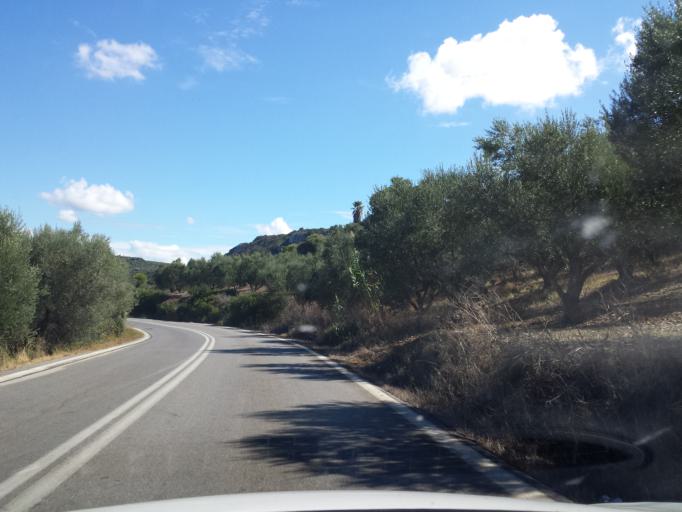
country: GR
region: Peloponnese
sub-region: Nomos Messinias
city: Pylos
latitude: 36.9316
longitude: 21.7323
